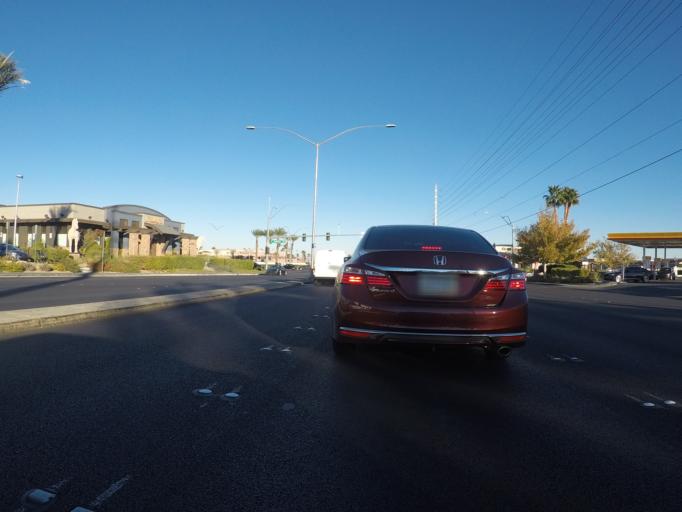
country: US
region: Nevada
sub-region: Clark County
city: Summerlin South
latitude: 36.1590
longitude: -115.2924
